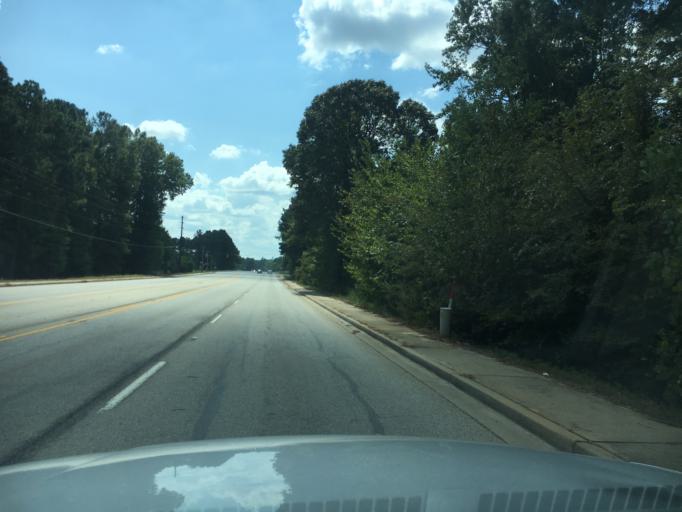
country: US
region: South Carolina
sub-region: Greenwood County
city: Greenwood
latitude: 34.2220
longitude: -82.2020
